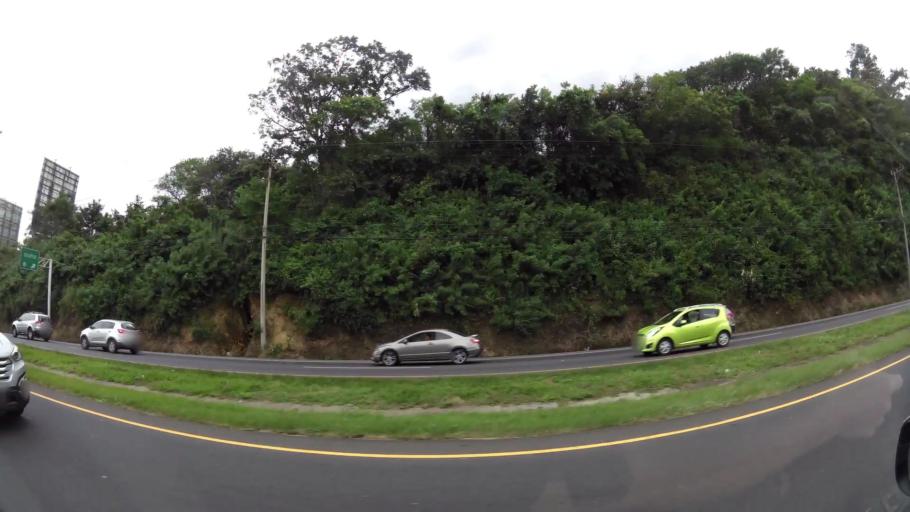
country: CR
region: San Jose
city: Santa Ana
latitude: 9.9450
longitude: -84.1660
